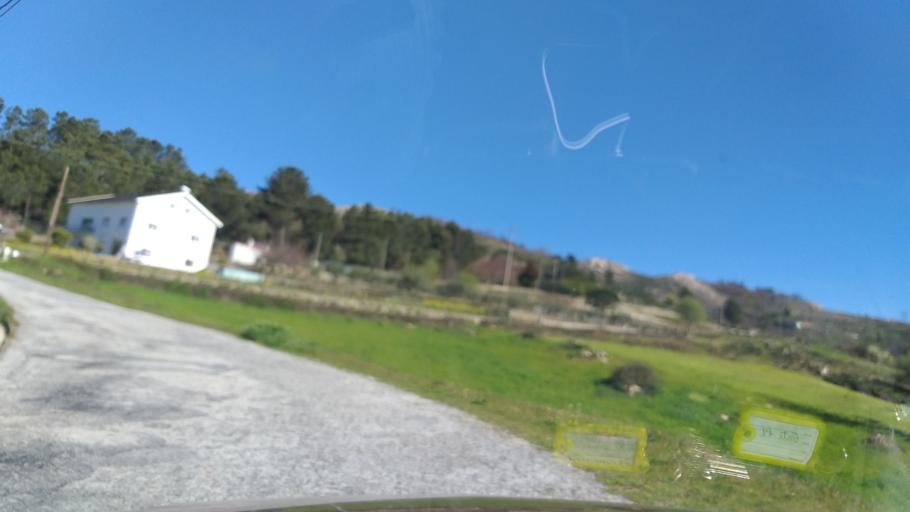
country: PT
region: Guarda
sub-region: Manteigas
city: Manteigas
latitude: 40.4900
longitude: -7.5852
